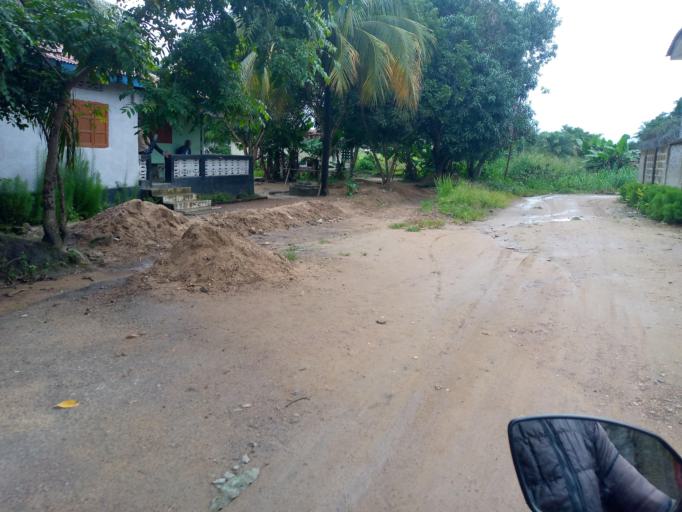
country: SL
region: Eastern Province
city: Kenema
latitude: 7.8469
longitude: -11.2078
